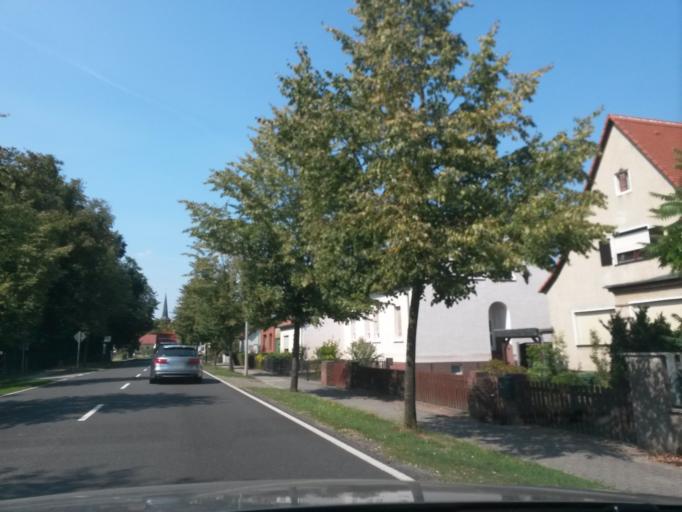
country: DE
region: Saxony-Anhalt
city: Jerichow
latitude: 52.4946
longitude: 12.0288
